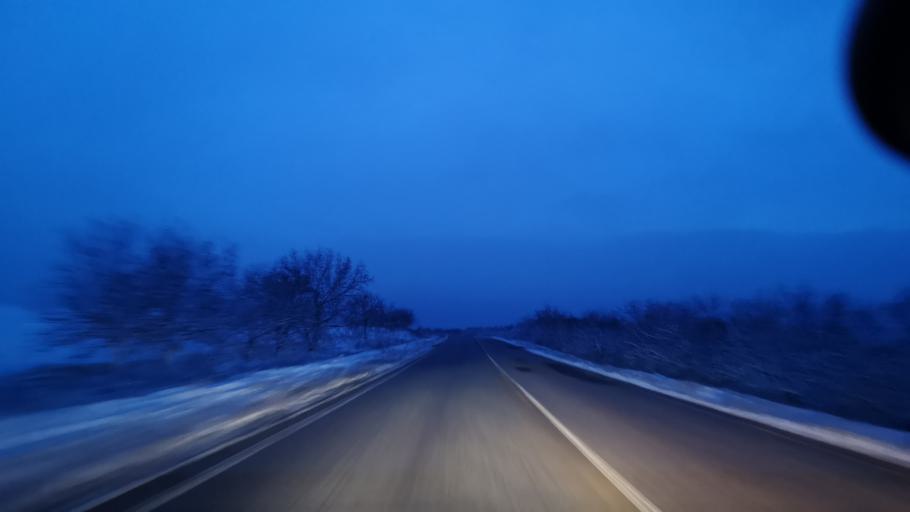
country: MD
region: Orhei
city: Orhei
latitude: 47.5570
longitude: 28.7978
